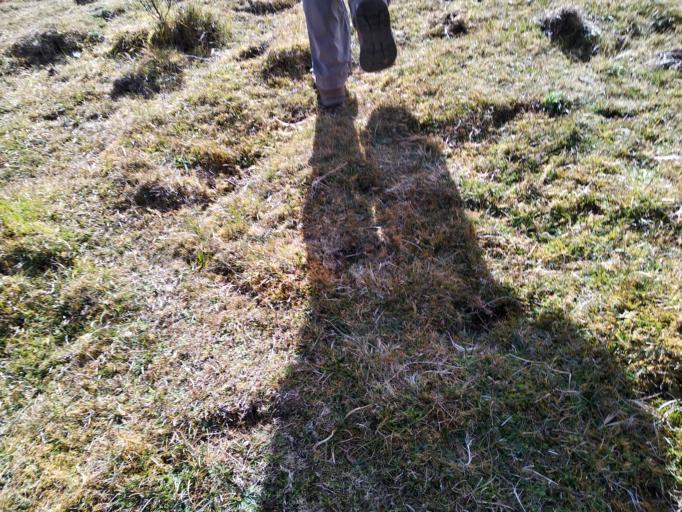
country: PE
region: Cusco
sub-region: Provincia de Urubamba
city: Ollantaytambo
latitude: -13.1247
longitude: -72.3356
